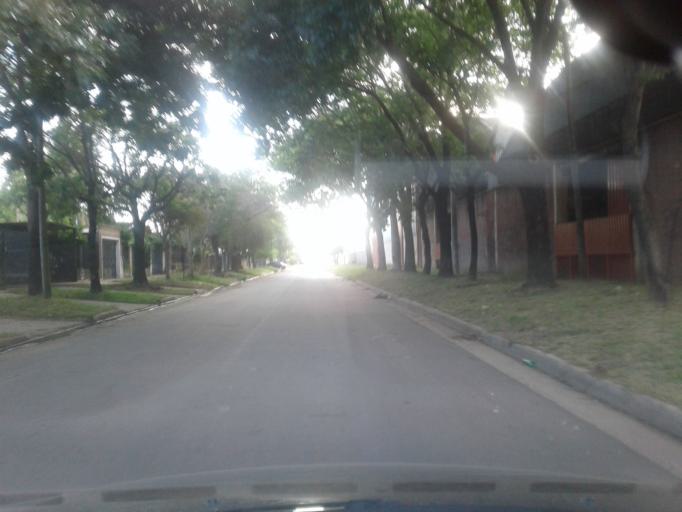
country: AR
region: Santa Fe
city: Granadero Baigorria
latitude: -32.8844
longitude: -60.7279
